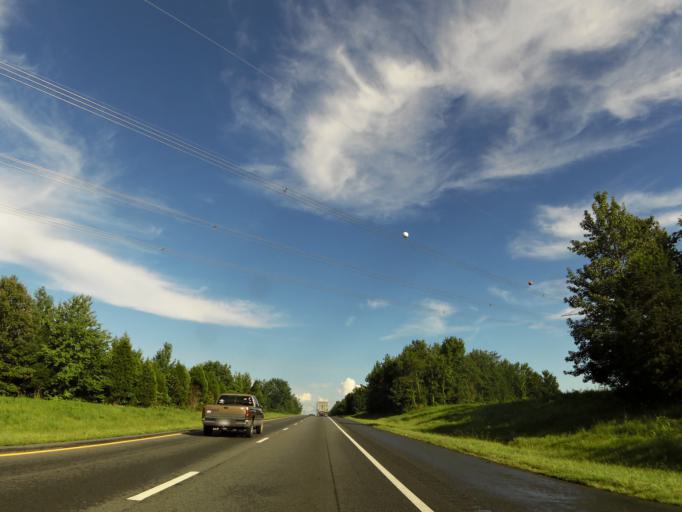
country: US
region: Kentucky
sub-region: Todd County
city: Guthrie
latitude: 36.5117
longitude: -87.2040
